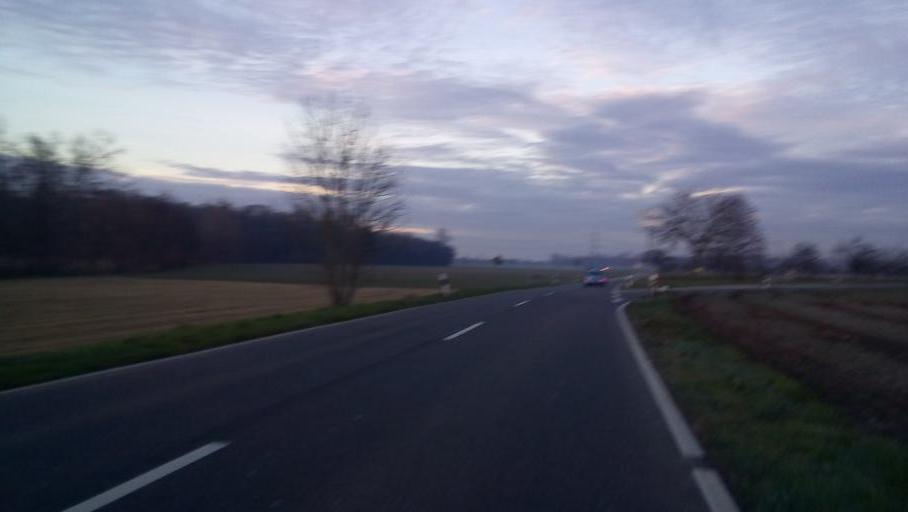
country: DE
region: Baden-Wuerttemberg
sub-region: Karlsruhe Region
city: Zell
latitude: 48.6979
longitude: 8.0671
